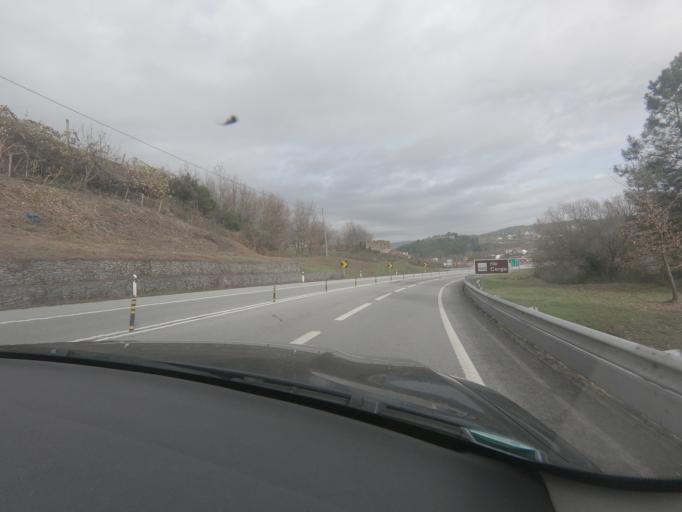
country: PT
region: Vila Real
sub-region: Vila Real
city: Vila Real
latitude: 41.3164
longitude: -7.7265
